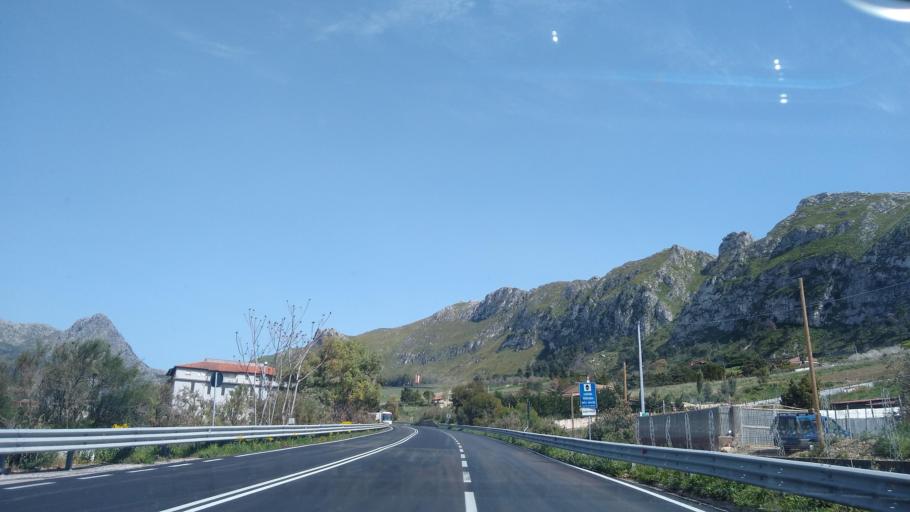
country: IT
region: Sicily
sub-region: Palermo
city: San Giuseppe Jato
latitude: 37.9750
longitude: 13.2052
